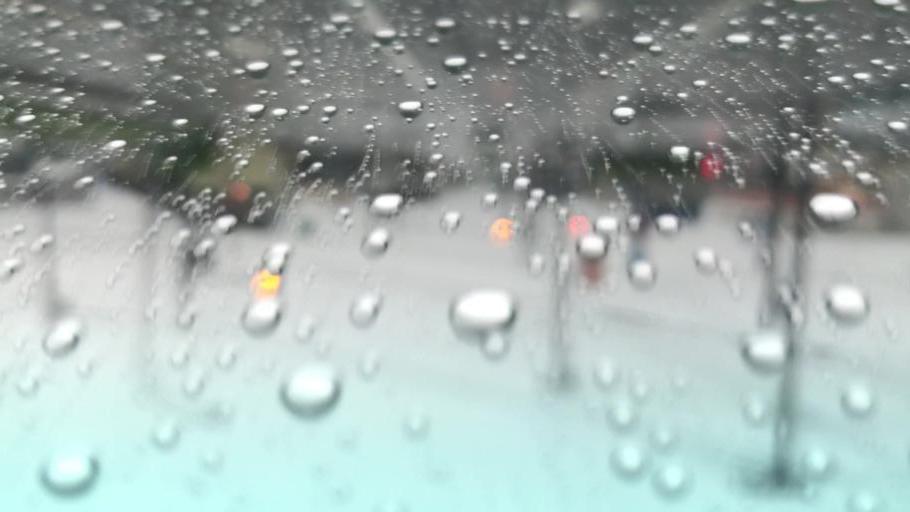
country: JP
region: Hokkaido
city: Nayoro
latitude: 44.2964
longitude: 142.4243
